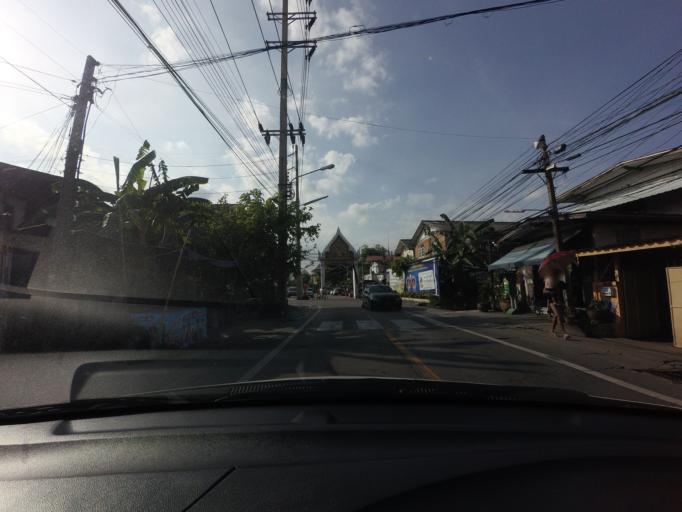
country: TH
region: Samut Prakan
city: Phra Pradaeng
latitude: 13.6666
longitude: 100.5290
